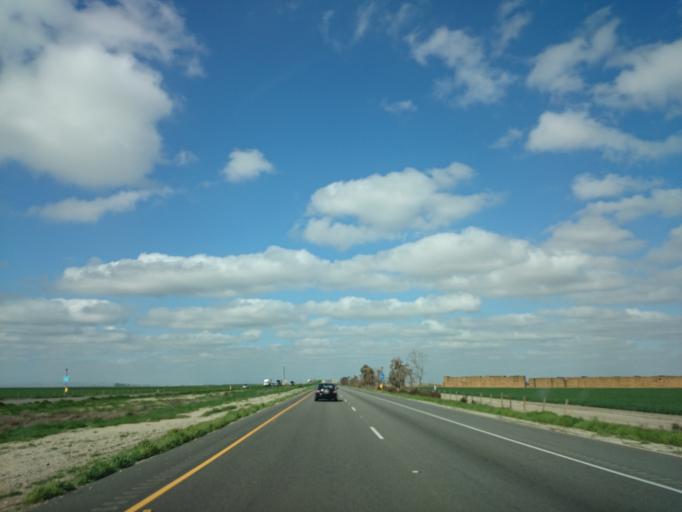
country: US
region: California
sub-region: Kern County
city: Greenfield
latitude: 35.1710
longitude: -119.1210
